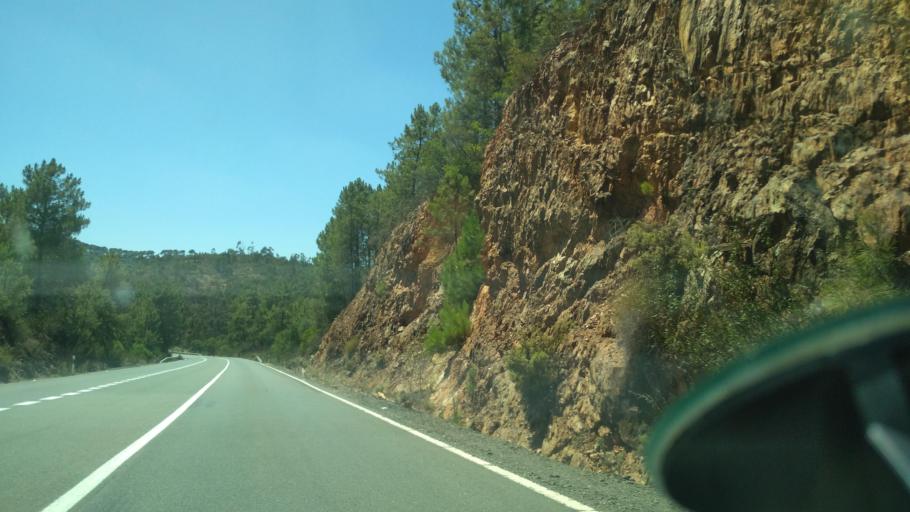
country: ES
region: Andalusia
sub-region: Provincia de Huelva
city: Campofrio
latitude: 37.7571
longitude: -6.5842
